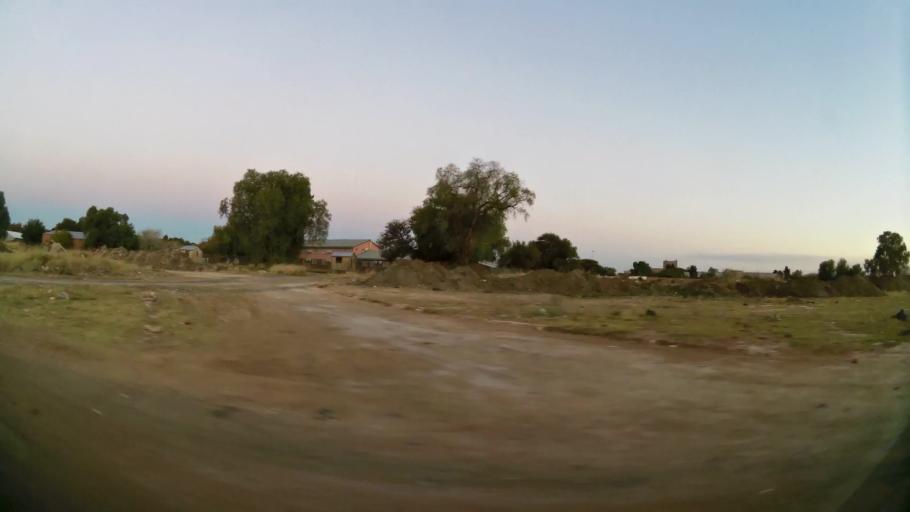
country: ZA
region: Northern Cape
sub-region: Frances Baard District Municipality
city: Kimberley
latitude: -28.7239
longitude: 24.7641
